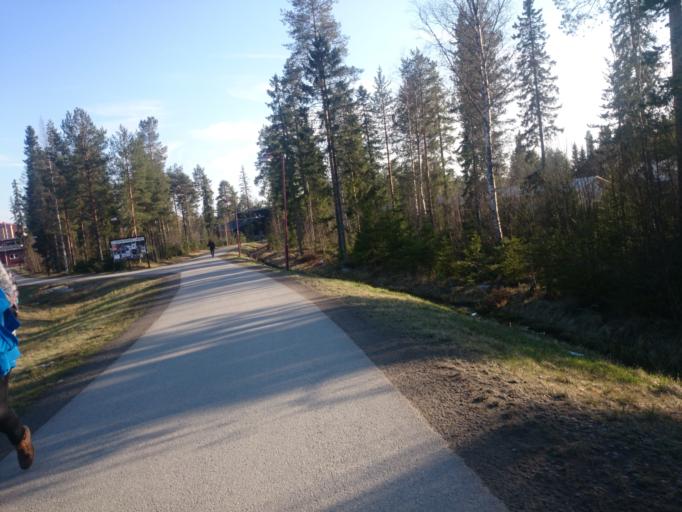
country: SE
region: Vaesterbotten
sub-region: Umea Kommun
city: Umea
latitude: 63.8204
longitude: 20.3179
